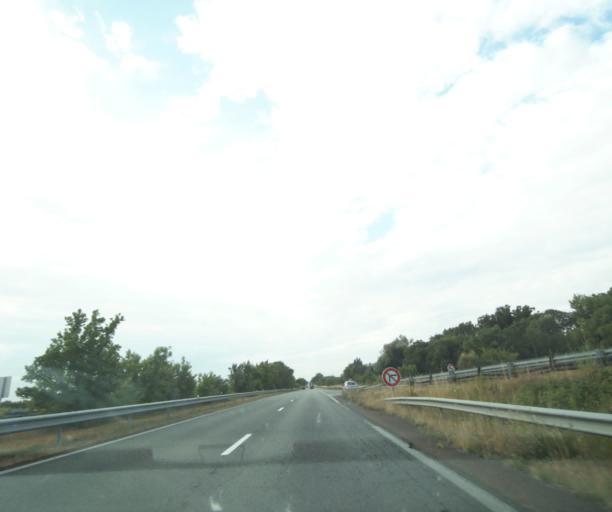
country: FR
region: Poitou-Charentes
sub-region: Departement de la Charente-Maritime
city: Chatelaillon-Plage
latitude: 46.0642
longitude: -1.0631
